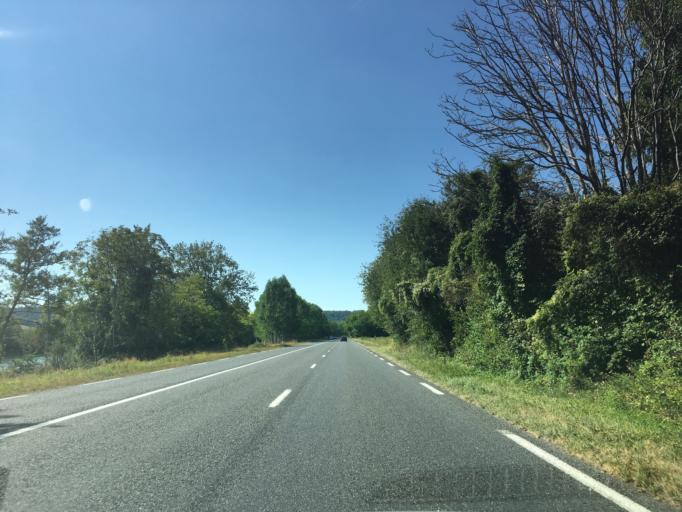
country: FR
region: Bourgogne
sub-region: Departement de l'Yonne
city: Saint-Julien-du-Sault
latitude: 48.0546
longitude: 3.3044
